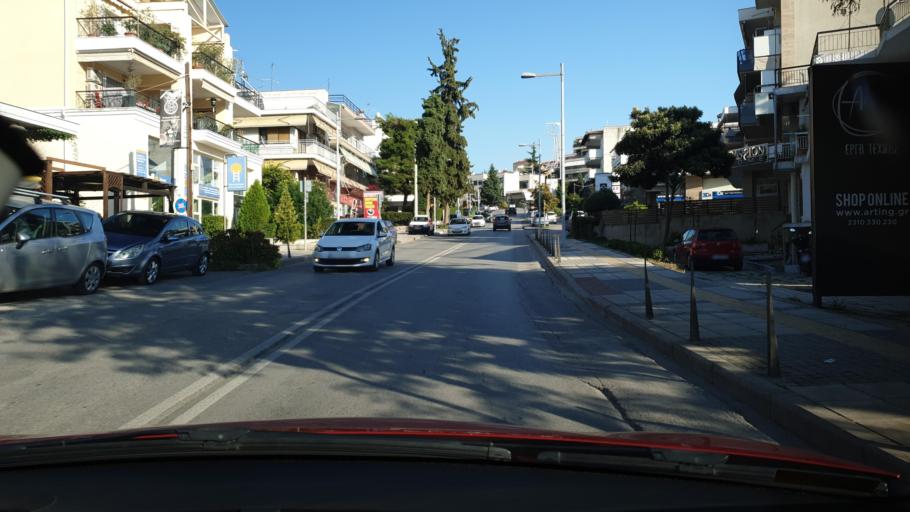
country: GR
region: Central Macedonia
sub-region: Nomos Thessalonikis
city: Pylaia
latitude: 40.6013
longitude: 22.9820
